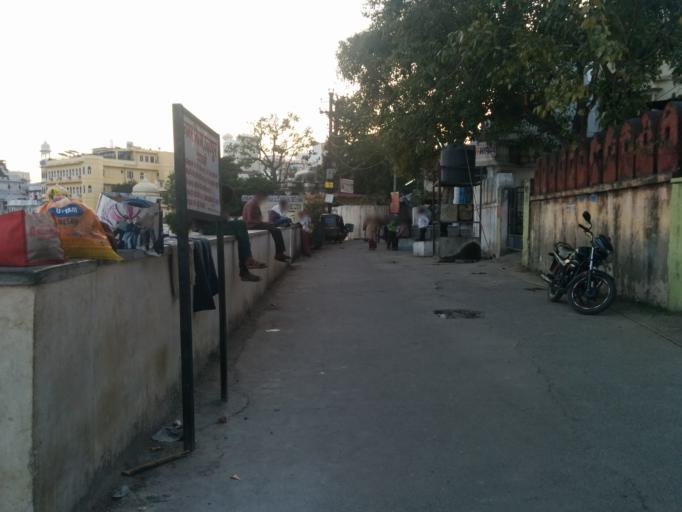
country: IN
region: Rajasthan
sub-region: Udaipur
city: Udaipur
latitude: 24.5813
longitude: 73.6809
